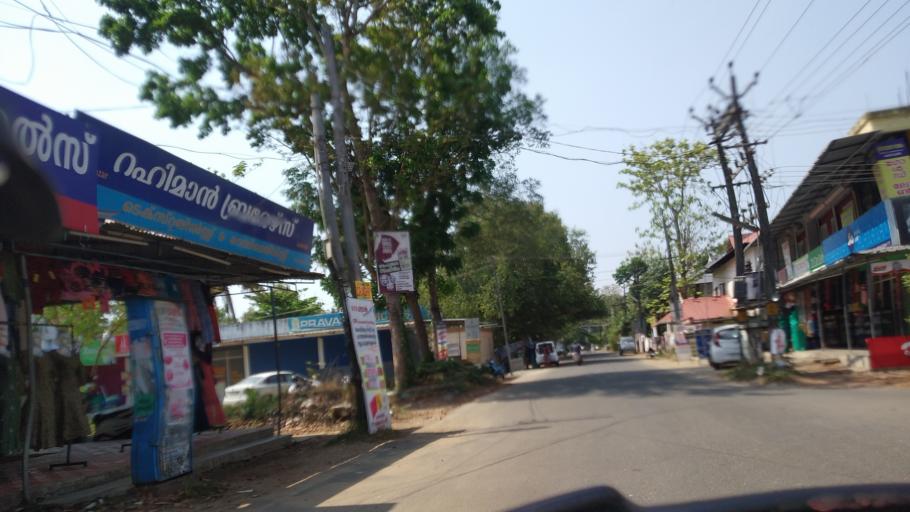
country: IN
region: Kerala
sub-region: Thrissur District
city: Kodungallur
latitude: 10.2108
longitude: 76.1627
